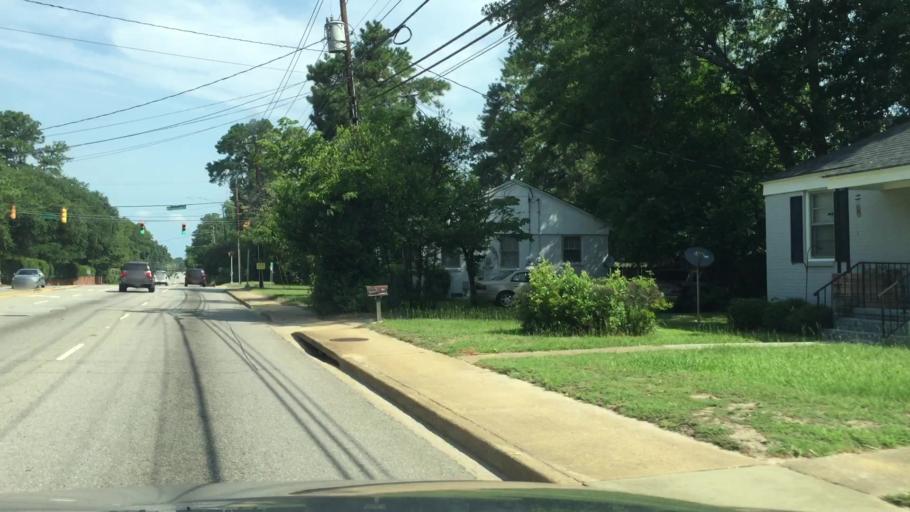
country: US
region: South Carolina
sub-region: Sumter County
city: Sumter
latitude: 33.9234
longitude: -80.3622
